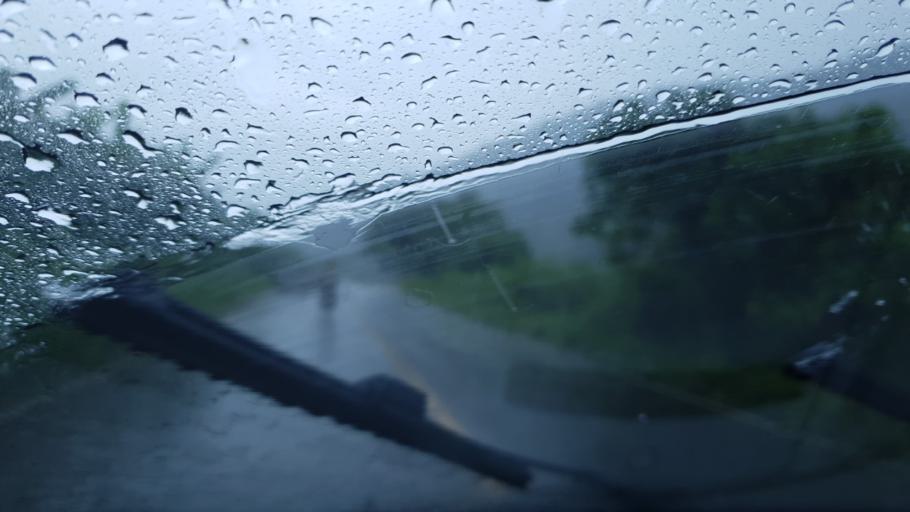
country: TH
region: Mae Hong Son
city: Khun Yuam
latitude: 18.6538
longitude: 97.9306
